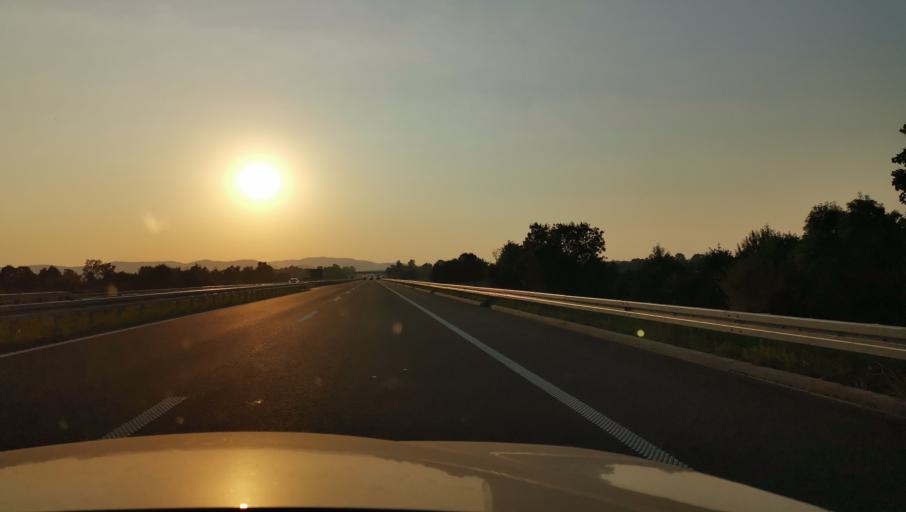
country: RS
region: Central Serbia
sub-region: Kolubarski Okrug
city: Lajkovac
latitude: 44.3498
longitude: 20.1614
